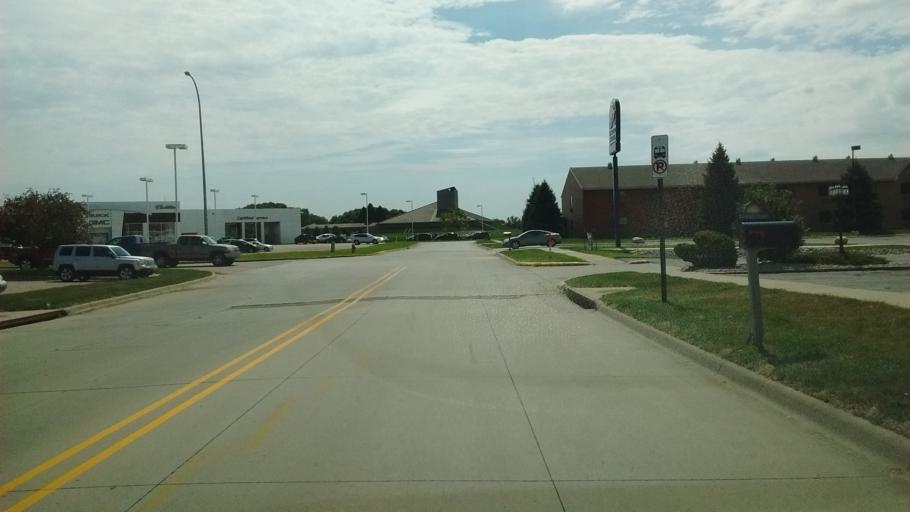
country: US
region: Iowa
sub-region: Woodbury County
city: Sergeant Bluff
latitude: 42.4351
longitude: -96.3681
